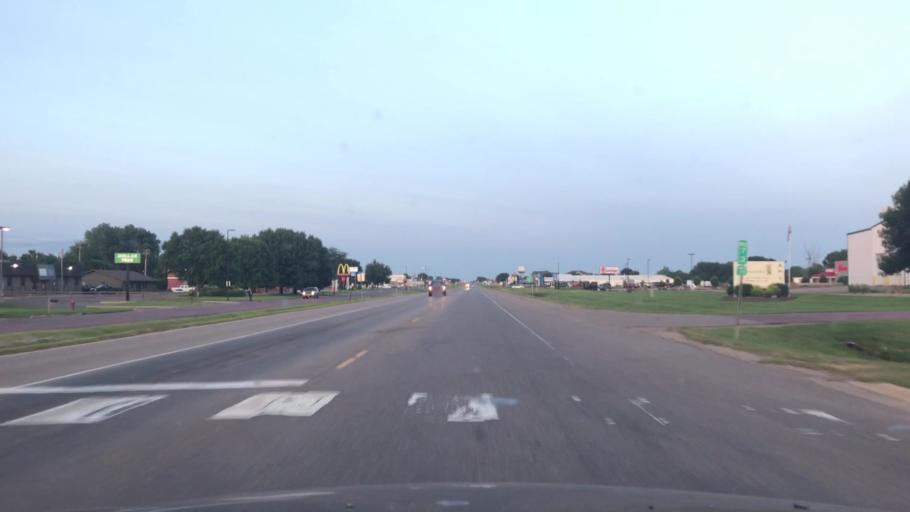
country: US
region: Minnesota
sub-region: Redwood County
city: Redwood Falls
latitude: 44.5414
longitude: -95.1005
